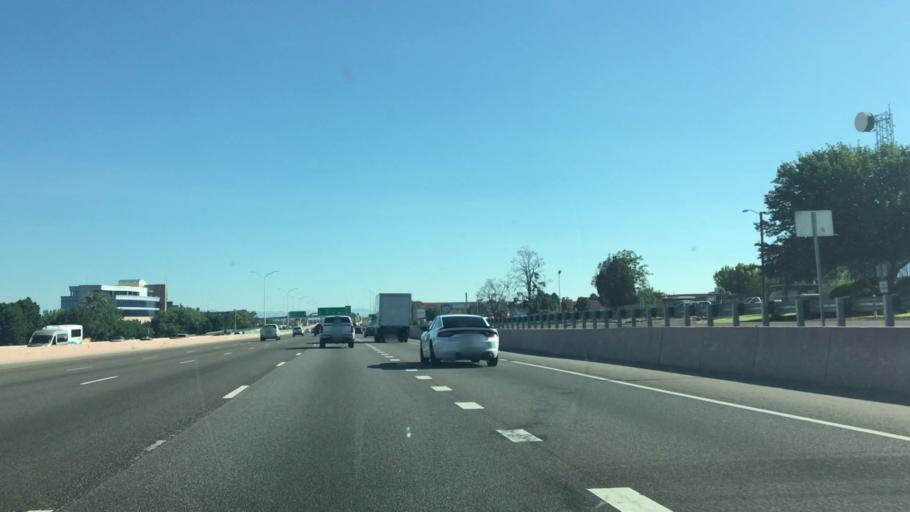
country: US
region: New Mexico
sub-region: Bernalillo County
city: North Valley
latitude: 35.1622
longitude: -106.5865
